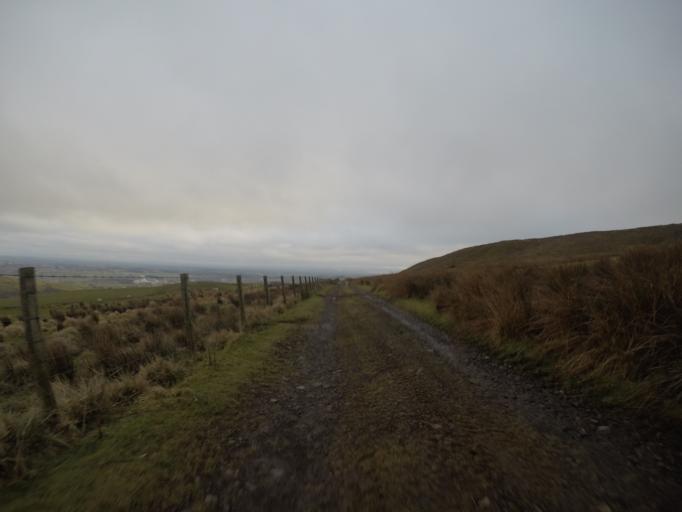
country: GB
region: Scotland
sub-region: North Ayrshire
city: Dalry
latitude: 55.7325
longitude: -4.7665
